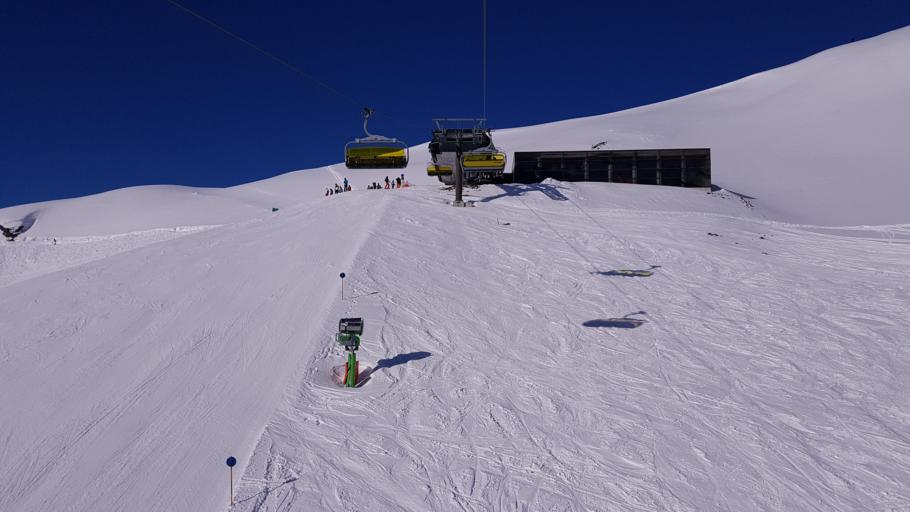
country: AT
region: Salzburg
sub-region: Politischer Bezirk Zell am See
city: Neukirchen am Grossvenediger
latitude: 47.2949
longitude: 12.2688
